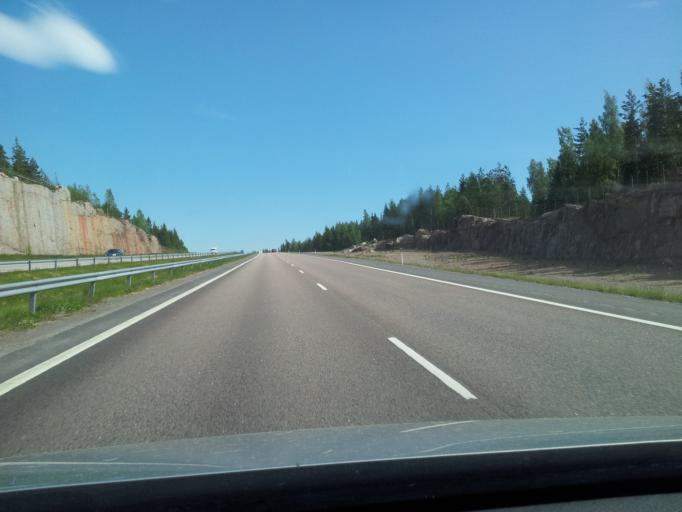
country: FI
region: Uusimaa
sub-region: Loviisa
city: Perna
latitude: 60.4856
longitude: 26.0159
